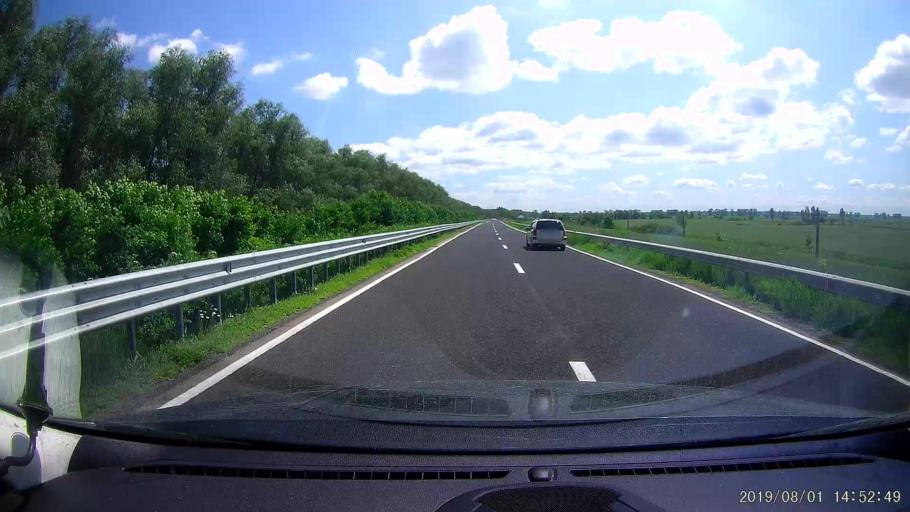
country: RO
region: Braila
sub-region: Comuna Vadeni
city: Vadeni
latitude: 45.3482
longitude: 28.0084
